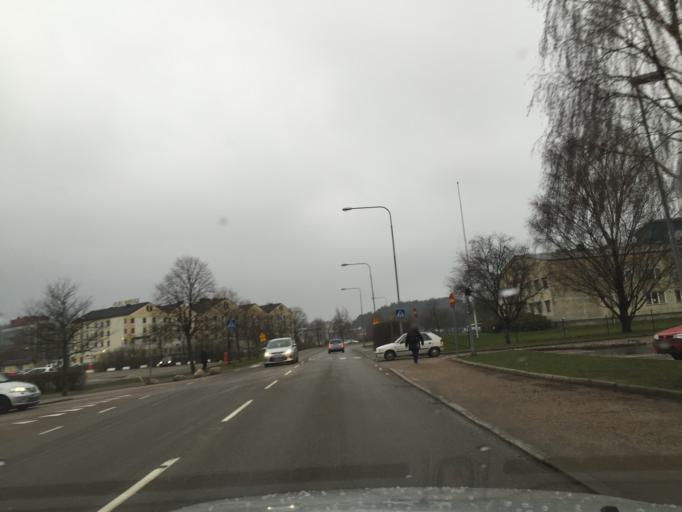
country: SE
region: Vaestra Goetaland
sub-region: Uddevalla Kommun
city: Uddevalla
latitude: 58.3506
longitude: 11.9269
